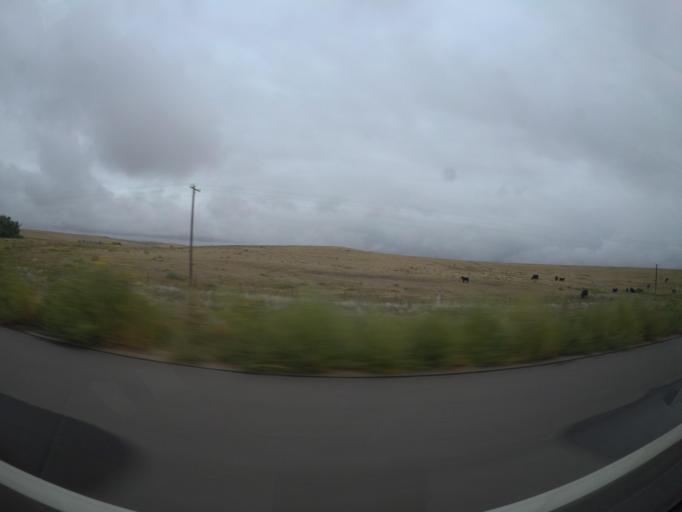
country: US
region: Colorado
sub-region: Lincoln County
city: Limon
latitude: 39.7399
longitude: -103.6871
